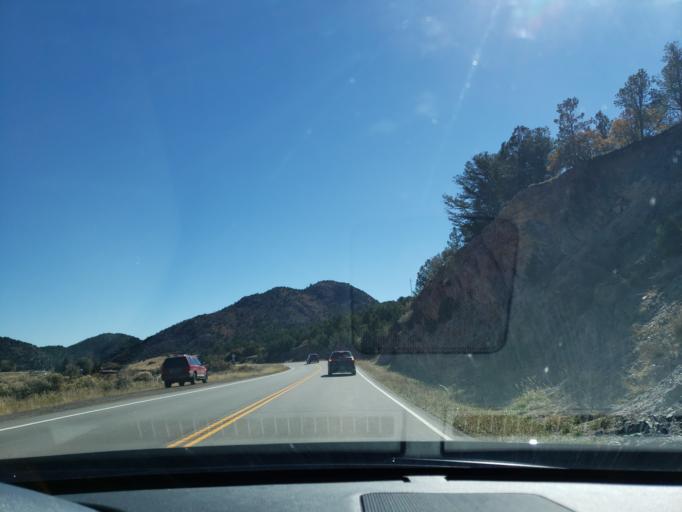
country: US
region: Colorado
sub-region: Fremont County
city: Canon City
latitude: 38.5884
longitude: -105.4222
